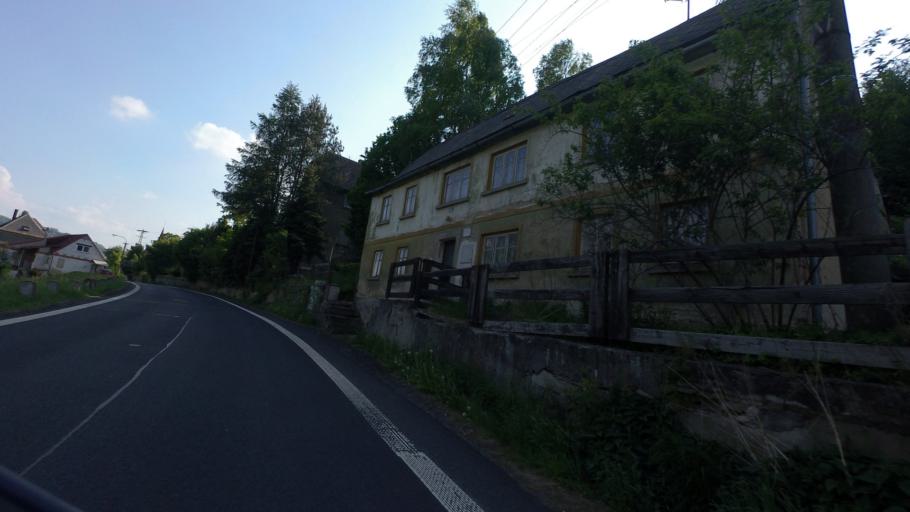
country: CZ
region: Ustecky
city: Dolni Poustevna
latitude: 50.9874
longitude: 14.2900
